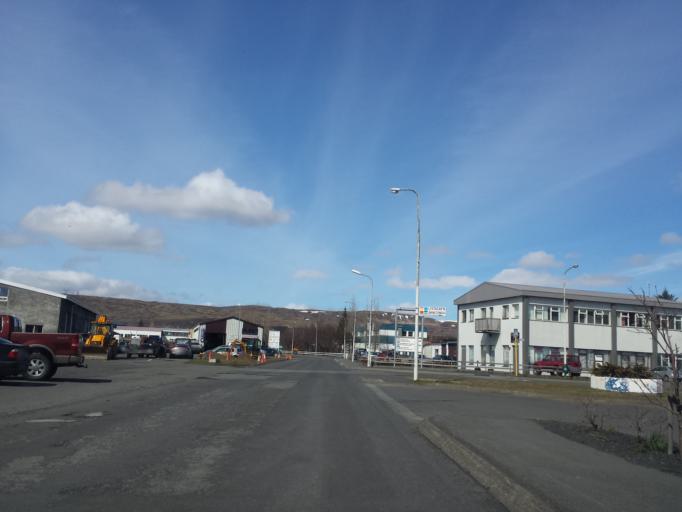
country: IS
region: South
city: Hveragerdi
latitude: 63.9960
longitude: -21.1855
